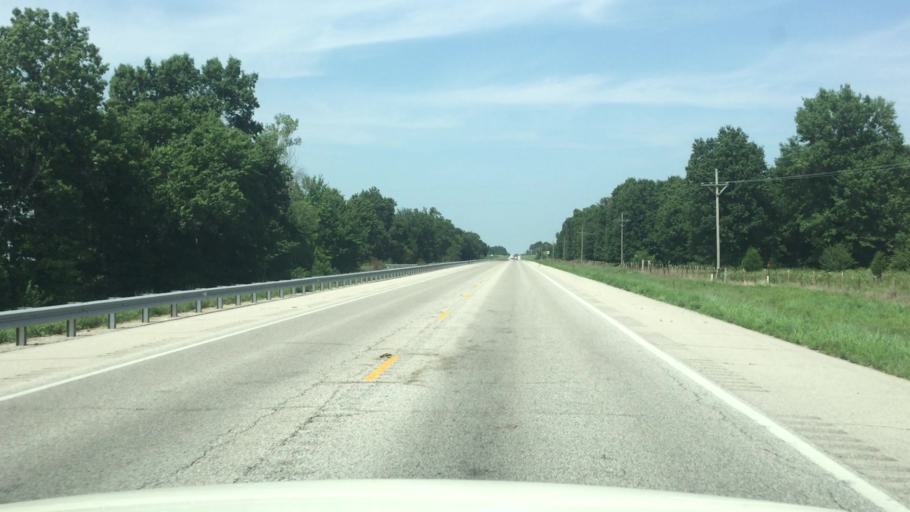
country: US
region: Kansas
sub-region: Cherokee County
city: Galena
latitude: 37.1357
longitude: -94.7043
